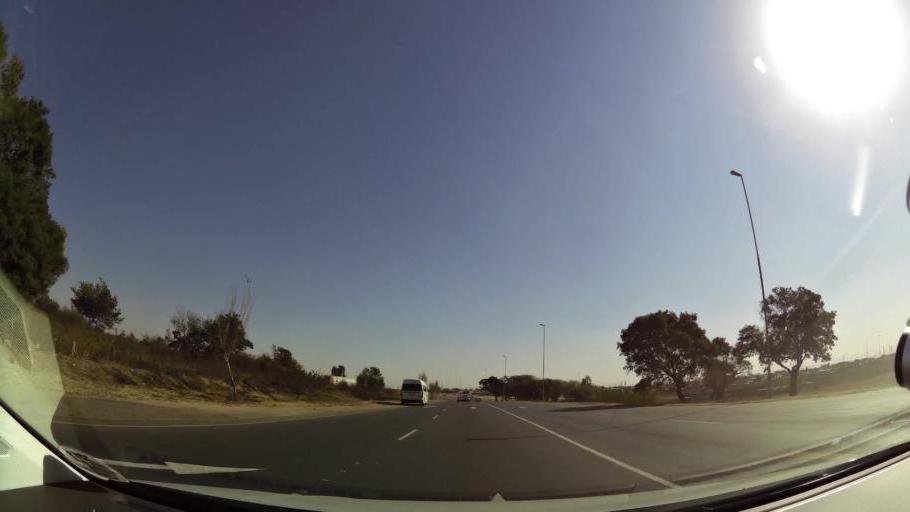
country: ZA
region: Gauteng
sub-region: Ekurhuleni Metropolitan Municipality
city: Tembisa
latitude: -26.0289
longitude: 28.2432
